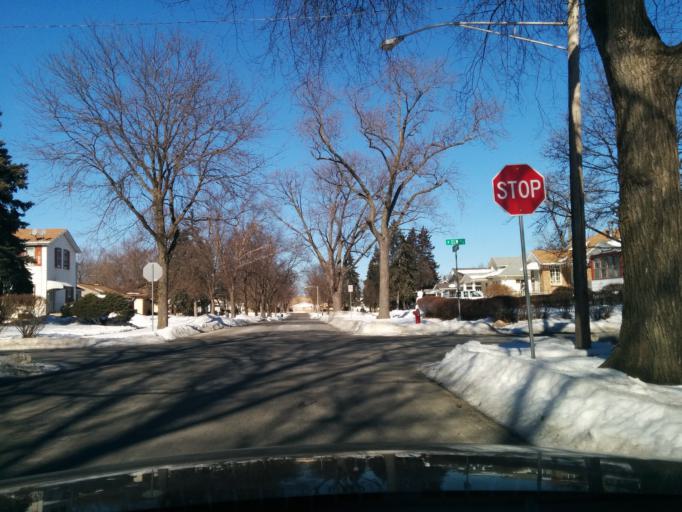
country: US
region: Illinois
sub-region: DuPage County
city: Villa Park
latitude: 41.8924
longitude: -87.9856
